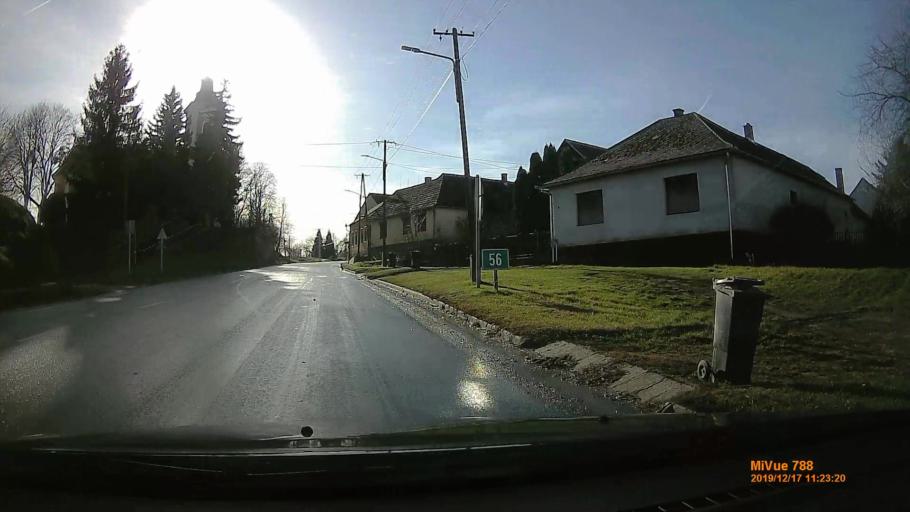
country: HU
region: Somogy
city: Kaposvar
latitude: 46.5059
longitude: 17.8188
